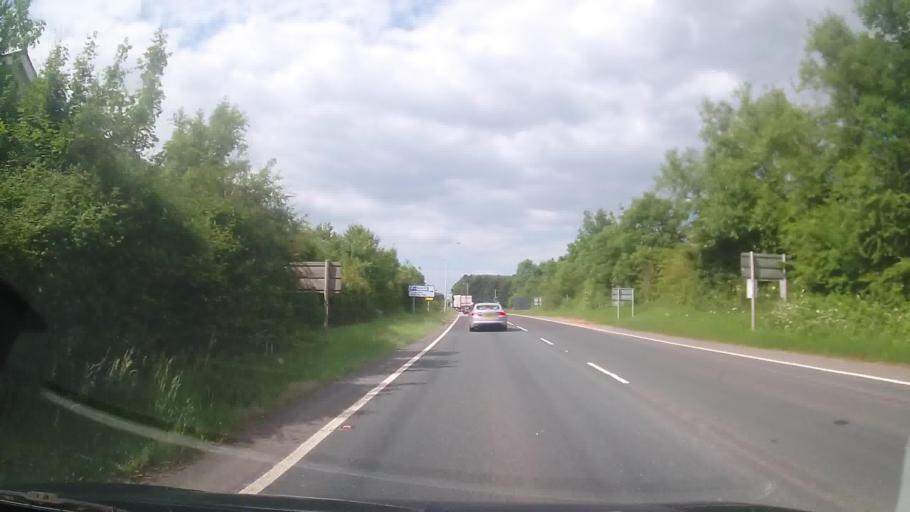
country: GB
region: England
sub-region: Shropshire
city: Ludlow
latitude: 52.3630
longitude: -2.6953
